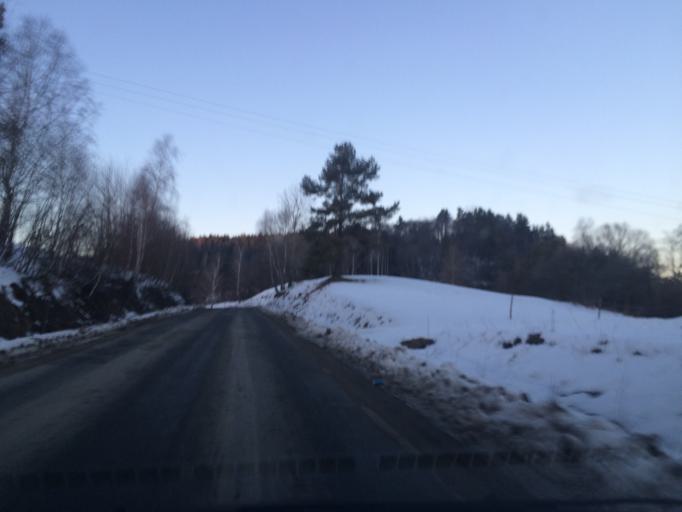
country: PL
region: Subcarpathian Voivodeship
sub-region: Powiat bieszczadzki
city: Ustrzyki Dolne
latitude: 49.3873
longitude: 22.6336
